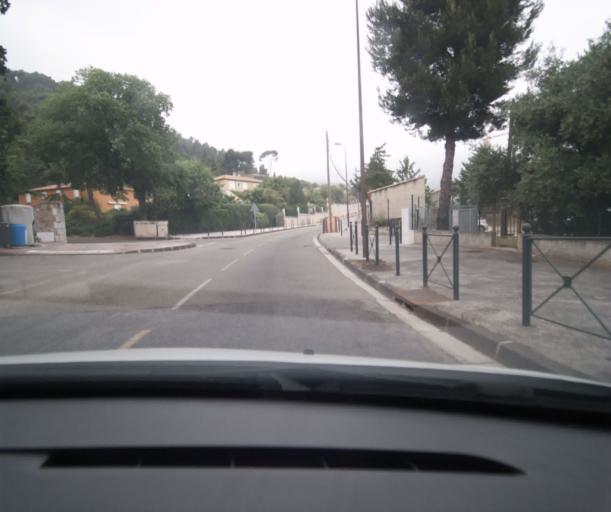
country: FR
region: Provence-Alpes-Cote d'Azur
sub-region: Departement du Var
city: La Valette-du-Var
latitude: 43.1394
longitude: 5.9785
